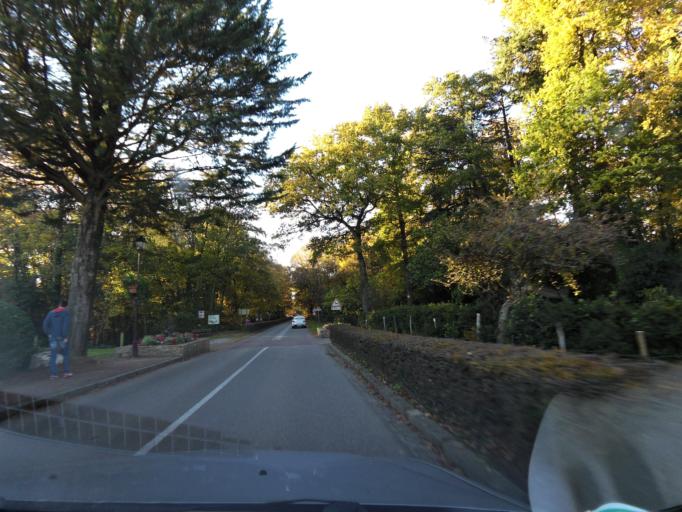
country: FR
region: Brittany
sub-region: Departement d'Ille-et-Vilaine
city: Pance
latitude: 47.8829
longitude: -1.6643
